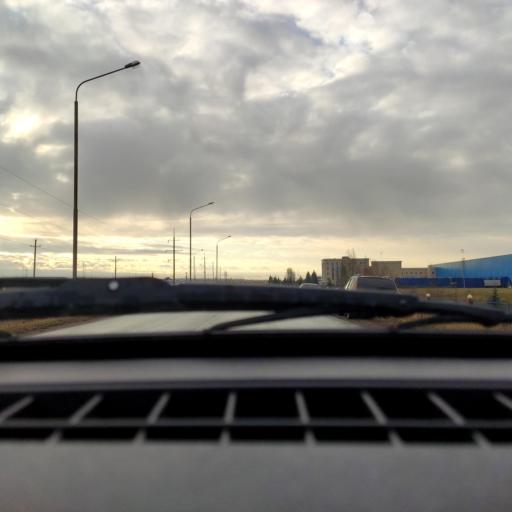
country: RU
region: Bashkortostan
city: Iglino
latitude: 54.7710
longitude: 56.2575
